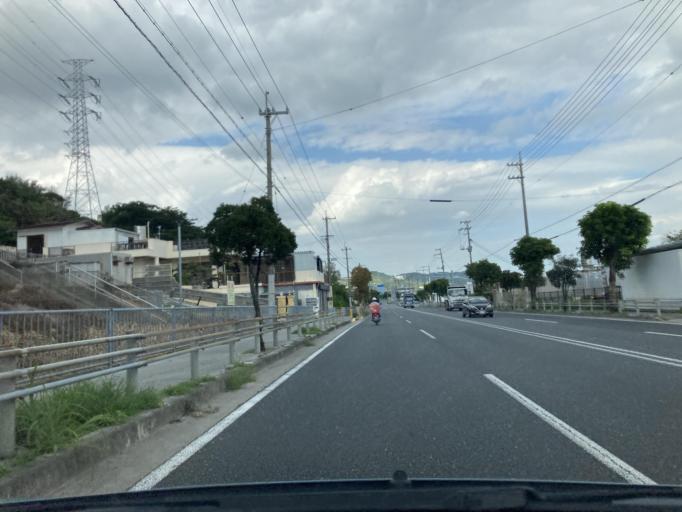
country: JP
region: Okinawa
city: Ginowan
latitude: 26.2513
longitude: 127.7831
